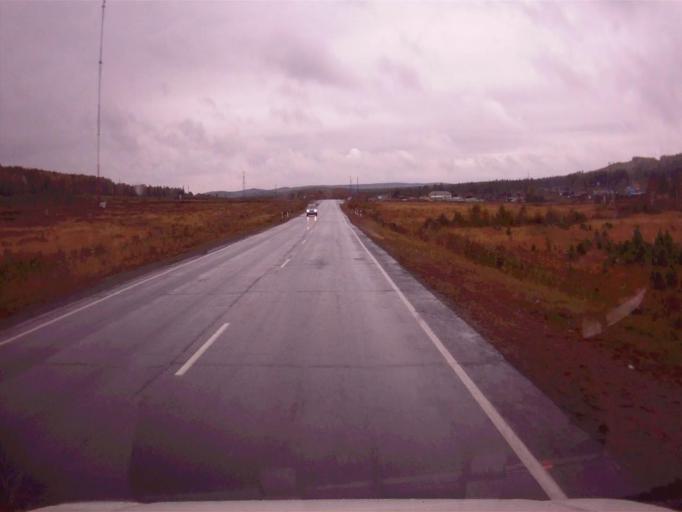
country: RU
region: Chelyabinsk
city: Verkhniy Ufaley
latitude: 56.0000
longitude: 60.3303
